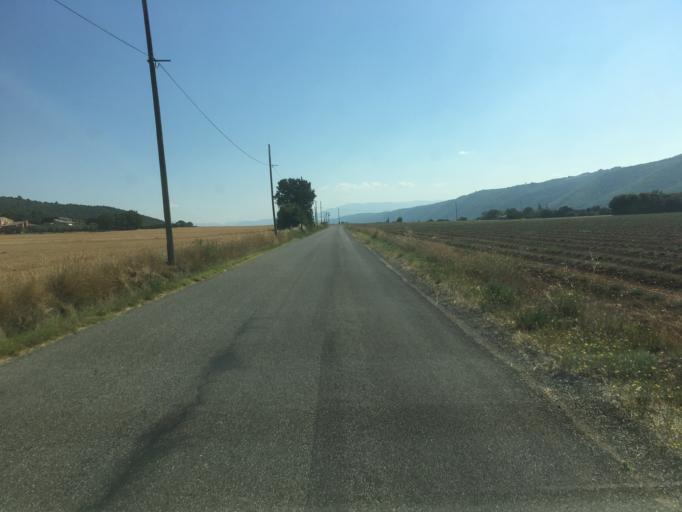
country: FR
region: Provence-Alpes-Cote d'Azur
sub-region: Departement des Alpes-de-Haute-Provence
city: Oraison
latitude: 43.8864
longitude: 5.9329
